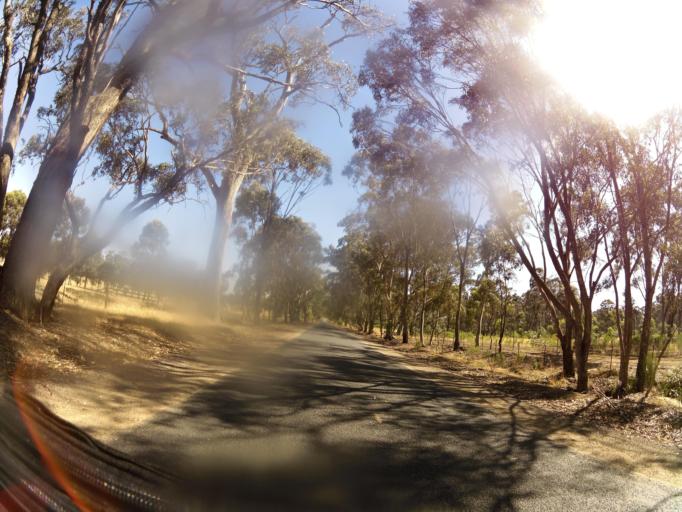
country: AU
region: Victoria
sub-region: Campaspe
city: Kyabram
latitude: -36.8716
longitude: 145.0863
